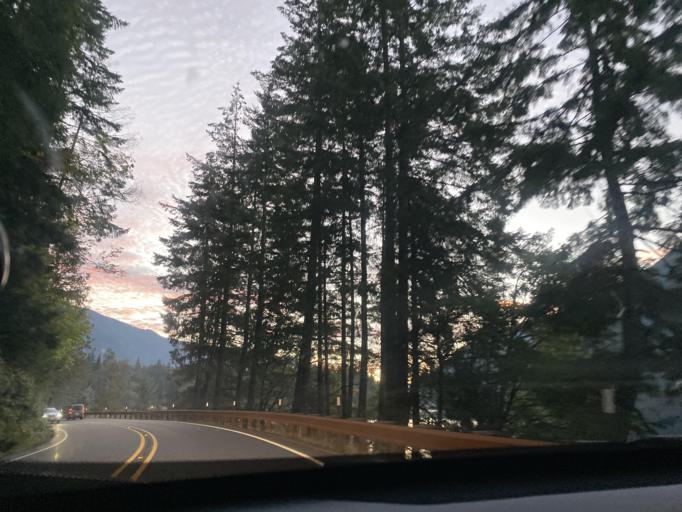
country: CA
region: British Columbia
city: Sooke
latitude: 48.0599
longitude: -123.7809
